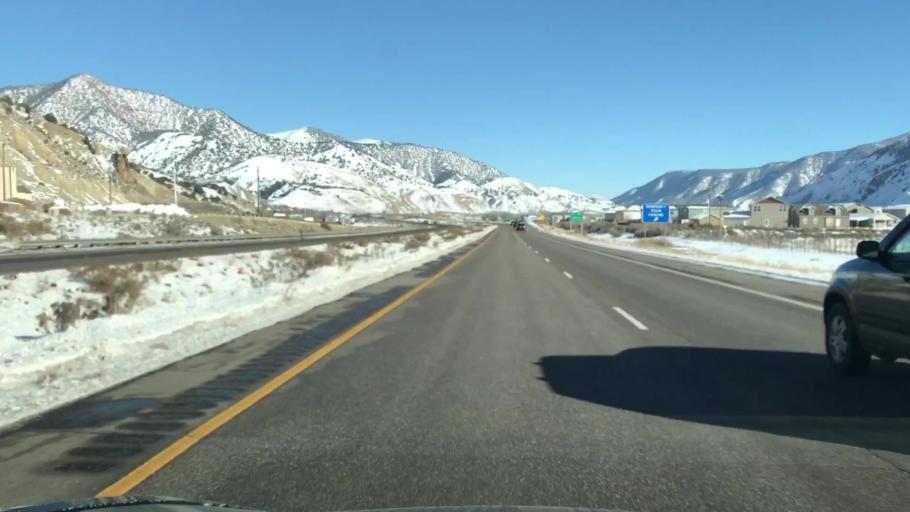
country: US
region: Colorado
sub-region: Eagle County
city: Gypsum
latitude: 39.6458
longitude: -107.0746
